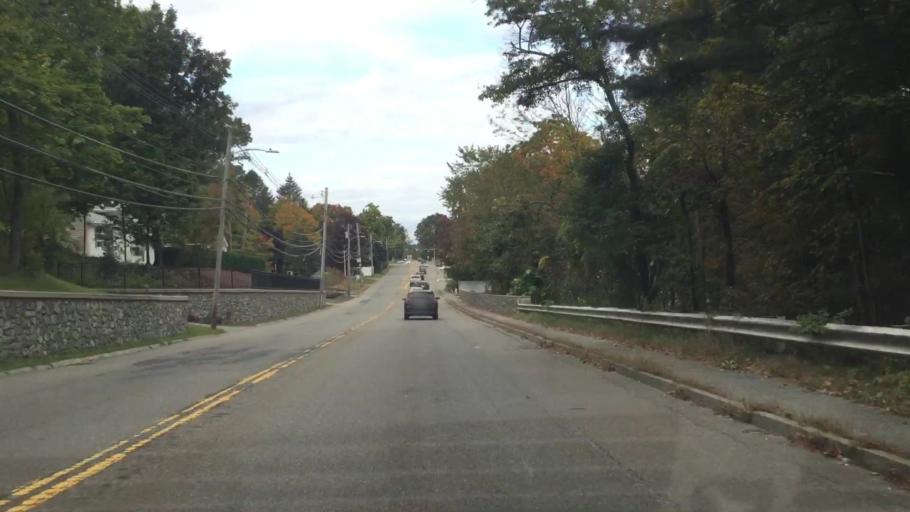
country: US
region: Massachusetts
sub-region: Essex County
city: Middleton
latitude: 42.5973
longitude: -71.0184
